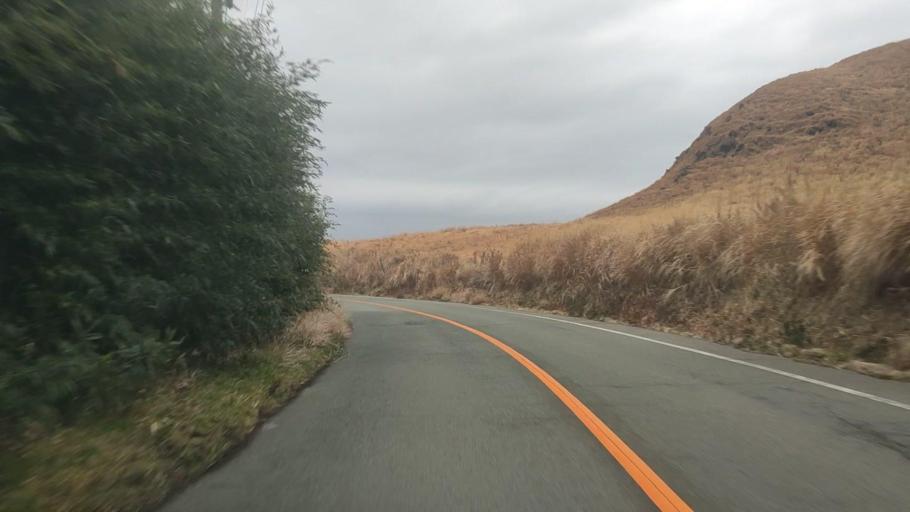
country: JP
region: Kumamoto
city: Aso
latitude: 32.9147
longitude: 131.1303
